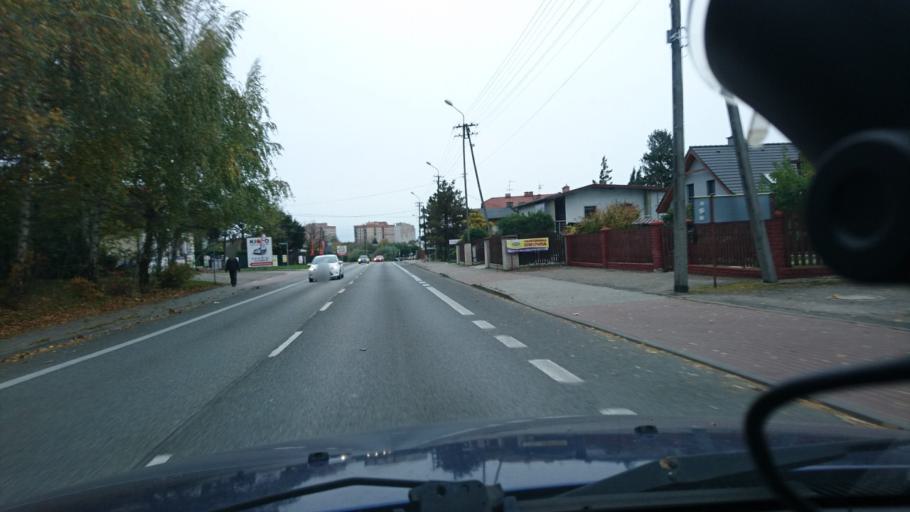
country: PL
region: Silesian Voivodeship
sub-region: Bielsko-Biala
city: Bielsko-Biala
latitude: 49.8098
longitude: 19.0155
